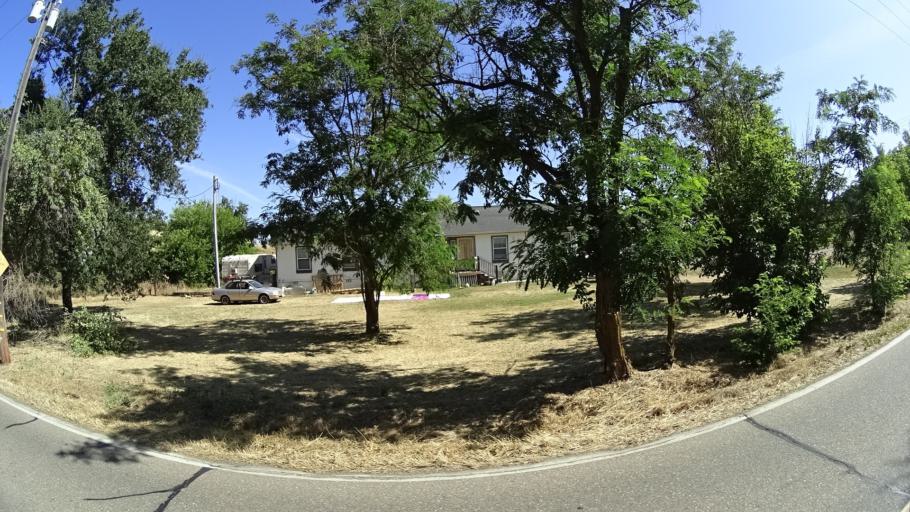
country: US
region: California
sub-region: Calaveras County
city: Rancho Calaveras
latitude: 38.0992
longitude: -120.8793
